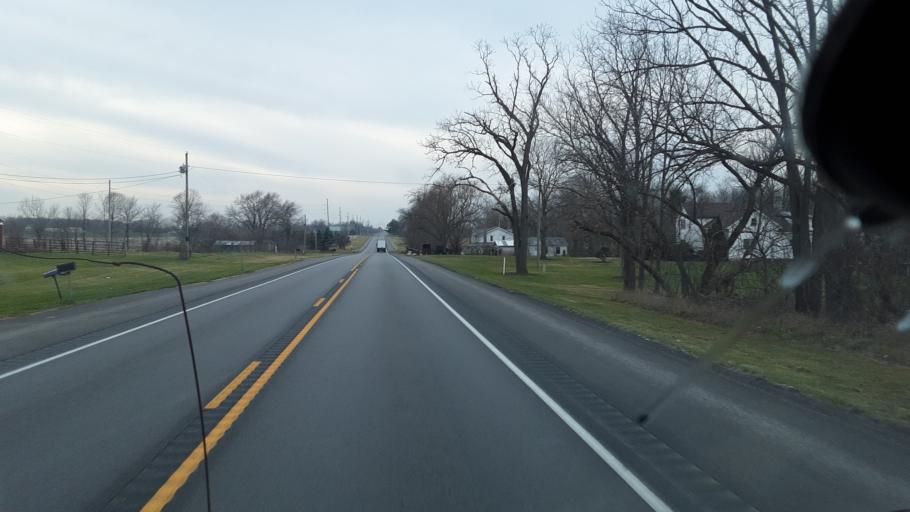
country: US
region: Indiana
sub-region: LaGrange County
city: Lagrange
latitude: 41.6421
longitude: -85.3366
